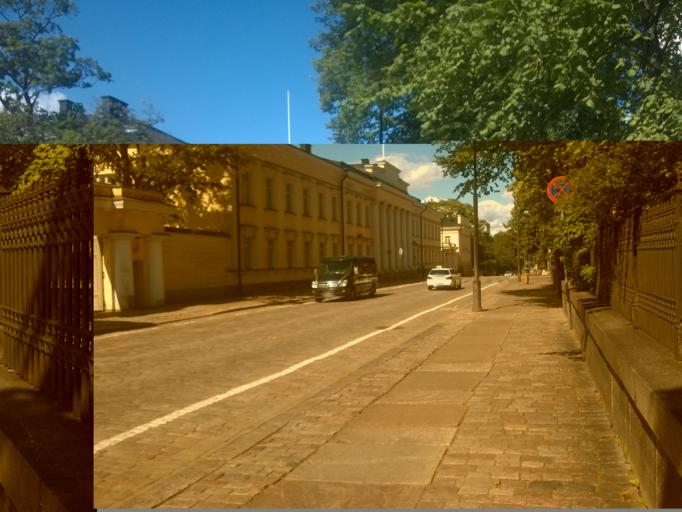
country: FI
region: Uusimaa
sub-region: Helsinki
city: Helsinki
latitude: 60.1709
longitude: 24.9509
